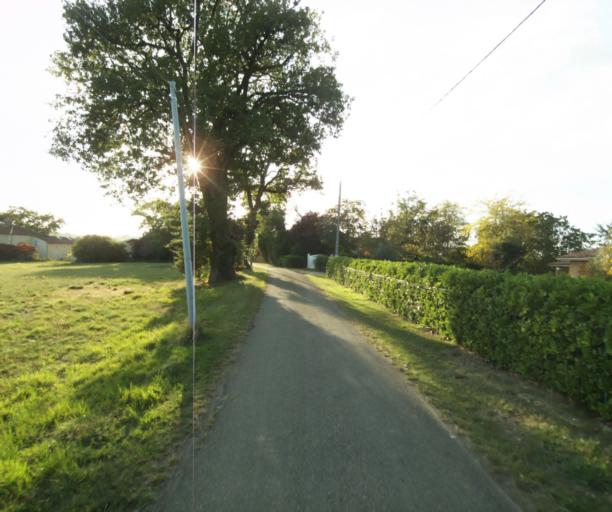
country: FR
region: Midi-Pyrenees
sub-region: Departement du Gers
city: Gondrin
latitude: 43.8831
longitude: 0.2595
